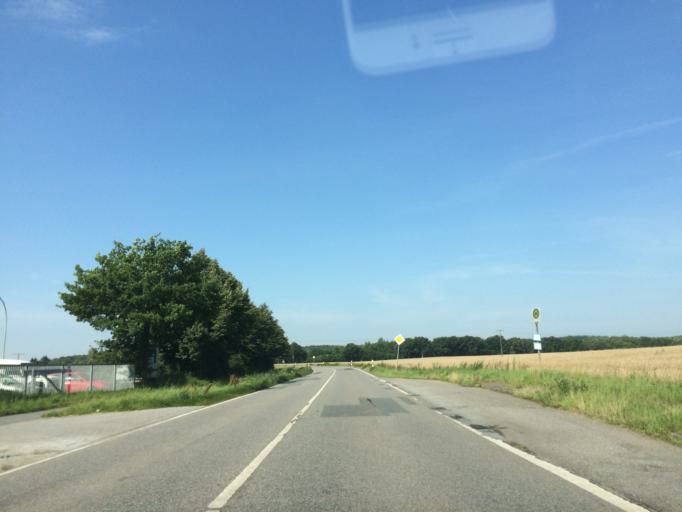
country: DE
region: Schleswig-Holstein
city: Pohnsdorf
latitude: 54.2397
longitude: 10.2493
